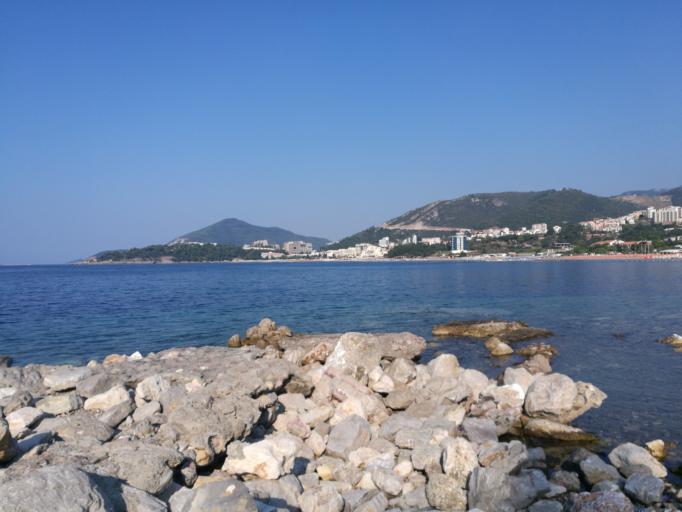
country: ME
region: Budva
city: Budva
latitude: 42.2775
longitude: 18.8805
